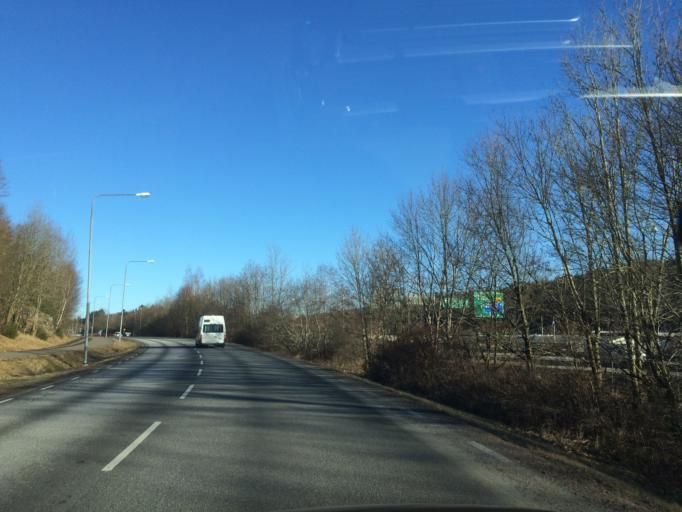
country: SE
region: Vaestra Goetaland
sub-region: Molndal
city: Kallered
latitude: 57.6135
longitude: 12.0434
